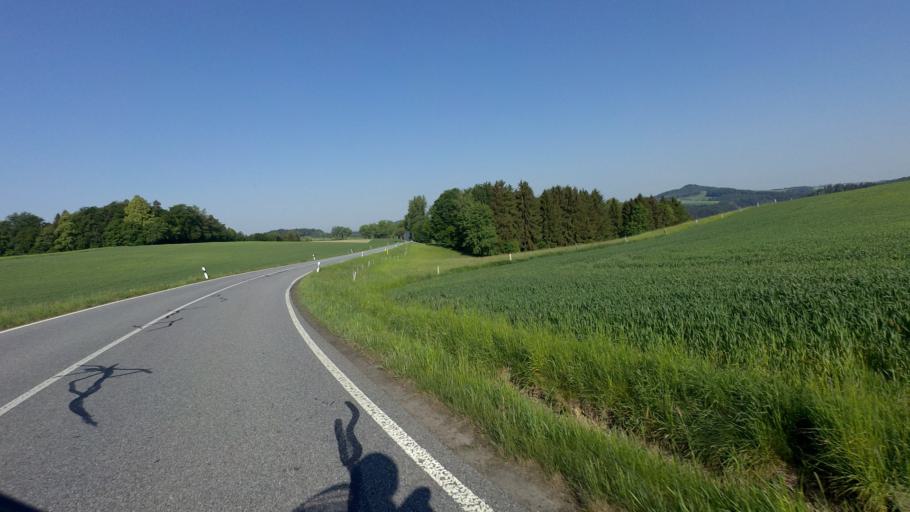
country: DE
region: Saxony
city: Bad Schandau
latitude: 50.9362
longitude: 14.1962
